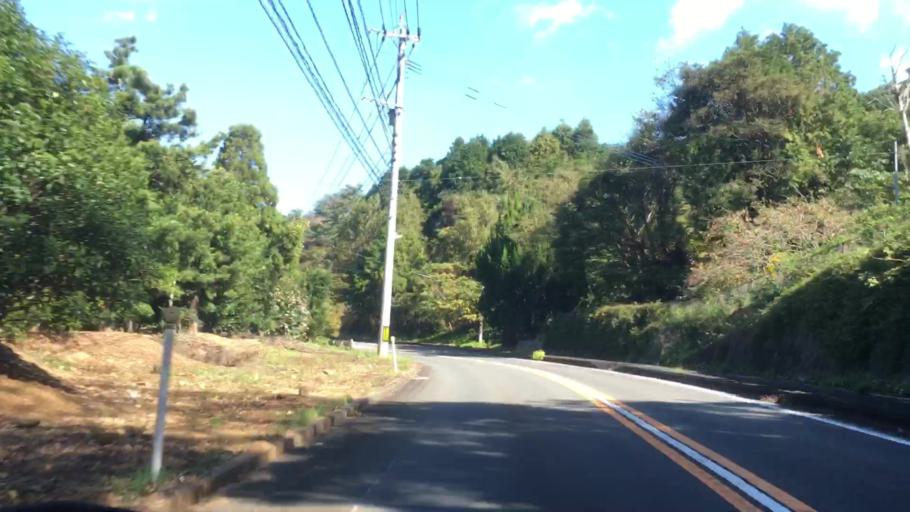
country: JP
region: Nagasaki
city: Sasebo
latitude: 33.0274
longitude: 129.6541
